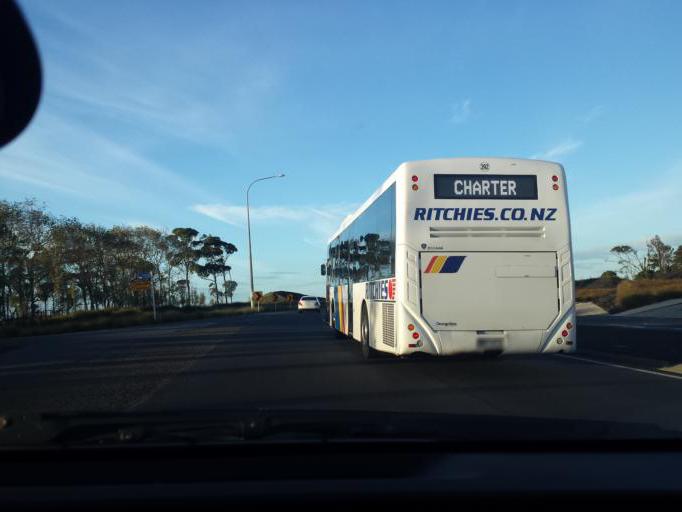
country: NZ
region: Auckland
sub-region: Auckland
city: Mangere
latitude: -36.9924
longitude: 174.7864
